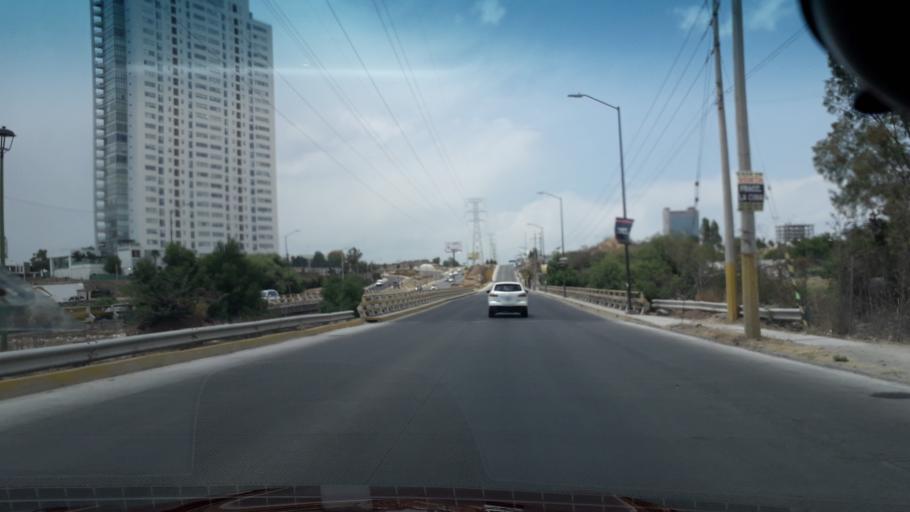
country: MX
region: Puebla
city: Tlazcalancingo
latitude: 19.0127
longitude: -98.2462
